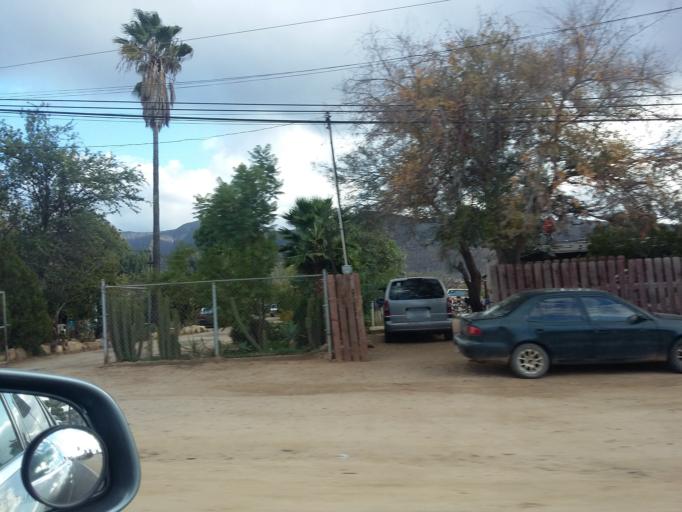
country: MX
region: Baja California
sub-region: Ensenada
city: Rancho Verde
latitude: 32.0915
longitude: -116.5799
